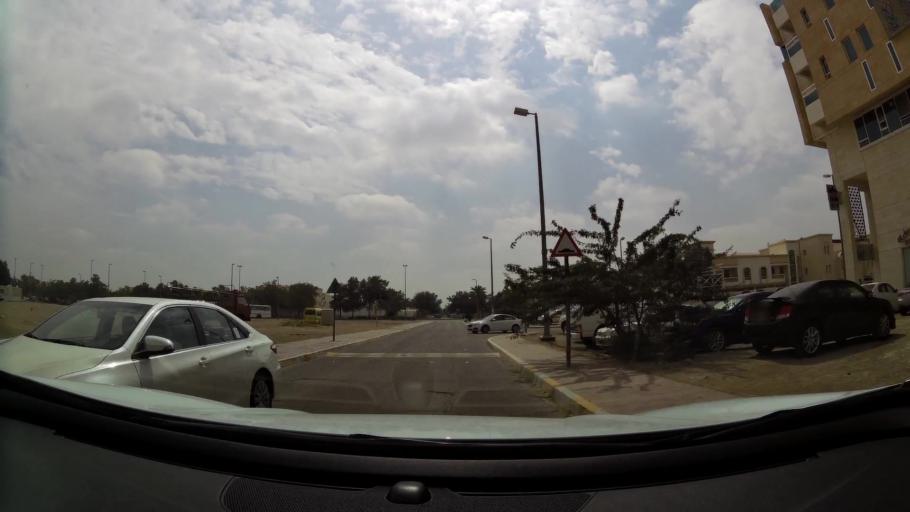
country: AE
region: Abu Dhabi
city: Al Ain
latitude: 24.2145
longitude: 55.7808
